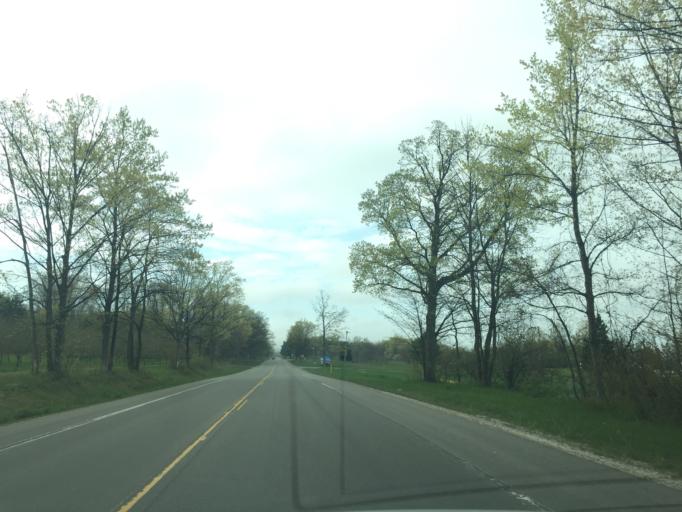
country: US
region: Michigan
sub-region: Leelanau County
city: Leland
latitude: 45.0740
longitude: -85.5892
